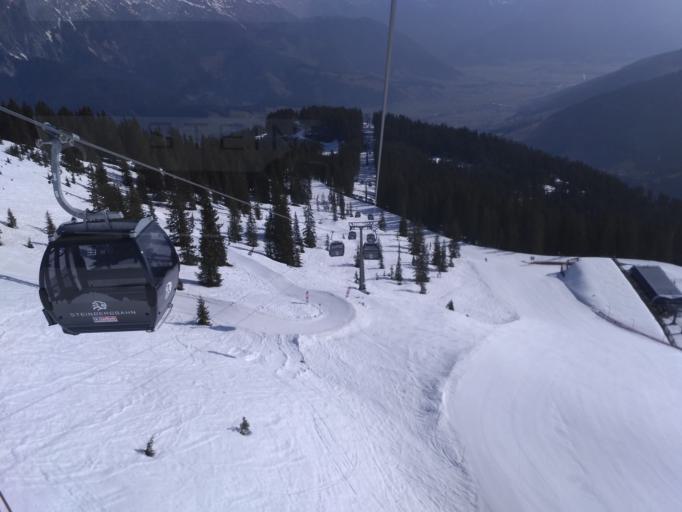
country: AT
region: Salzburg
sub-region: Politischer Bezirk Zell am See
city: Viehhofen
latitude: 47.4112
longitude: 12.7158
